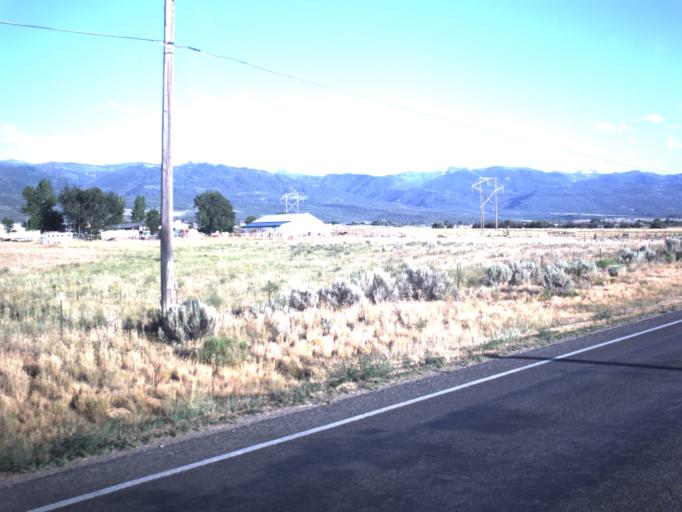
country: US
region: Utah
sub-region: Sanpete County
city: Mount Pleasant
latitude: 39.5699
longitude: -111.4555
